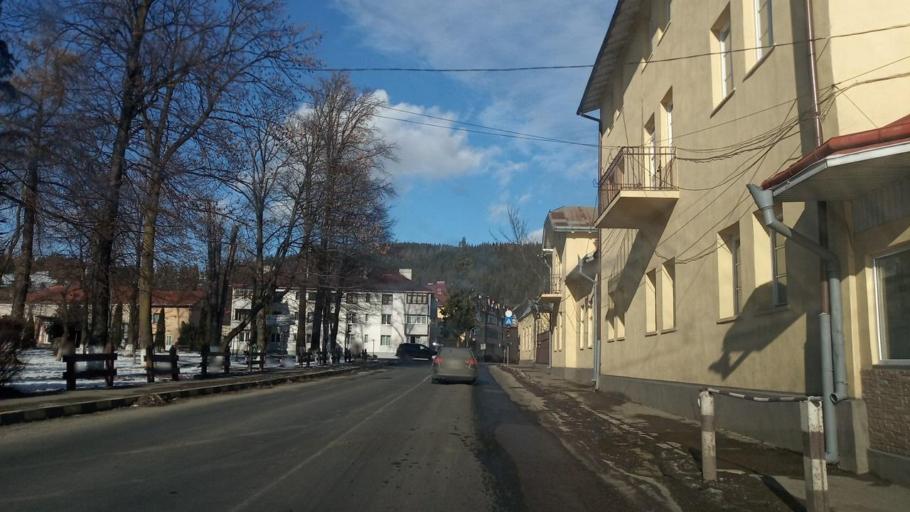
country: RO
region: Suceava
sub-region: Oras Gura Humorului
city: Gura Humorului
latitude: 47.5520
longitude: 25.8963
